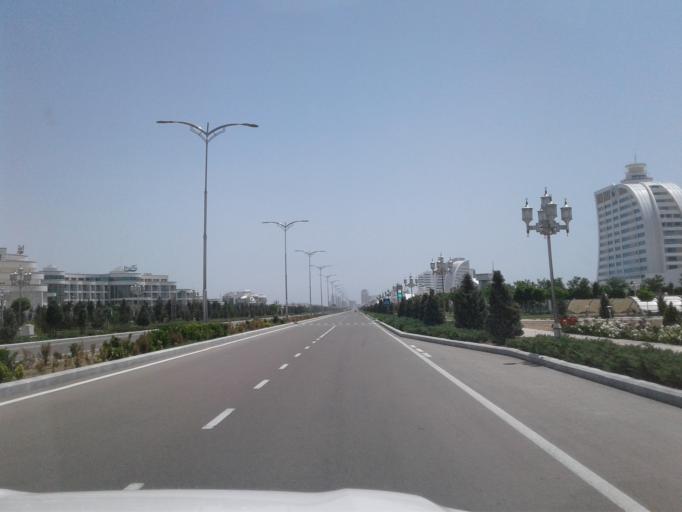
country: TM
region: Balkan
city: Turkmenbasy
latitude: 39.9829
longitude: 52.8264
